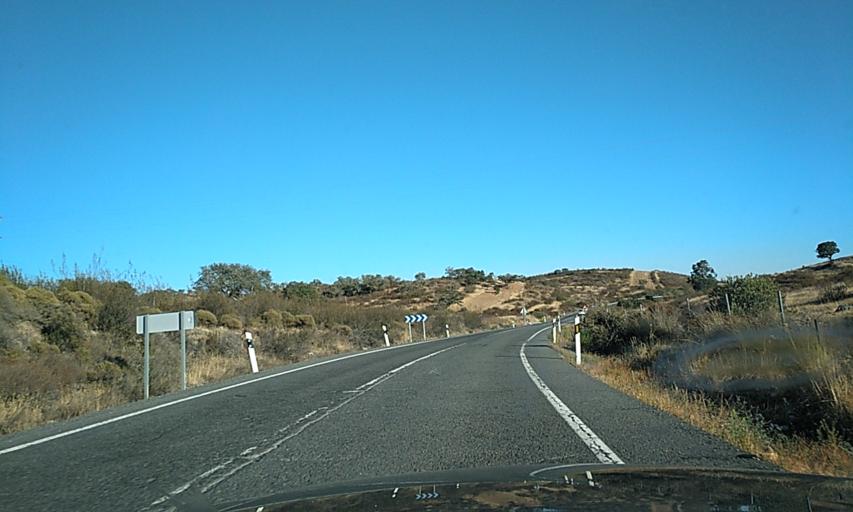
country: ES
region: Andalusia
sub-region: Provincia de Huelva
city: San Bartolome de la Torre
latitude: 37.4834
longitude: -7.1292
